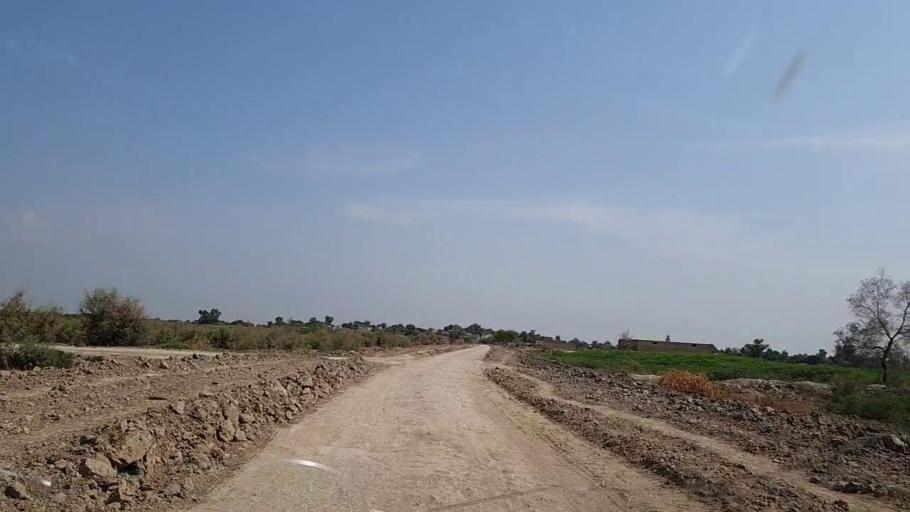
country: PK
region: Sindh
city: Khanpur
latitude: 27.7541
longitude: 69.3368
